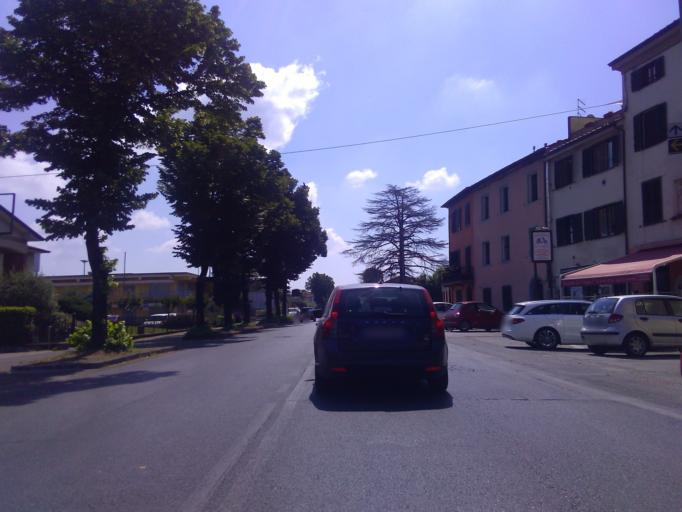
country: IT
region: Tuscany
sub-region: Provincia di Lucca
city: Lucca
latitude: 43.8479
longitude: 10.4696
